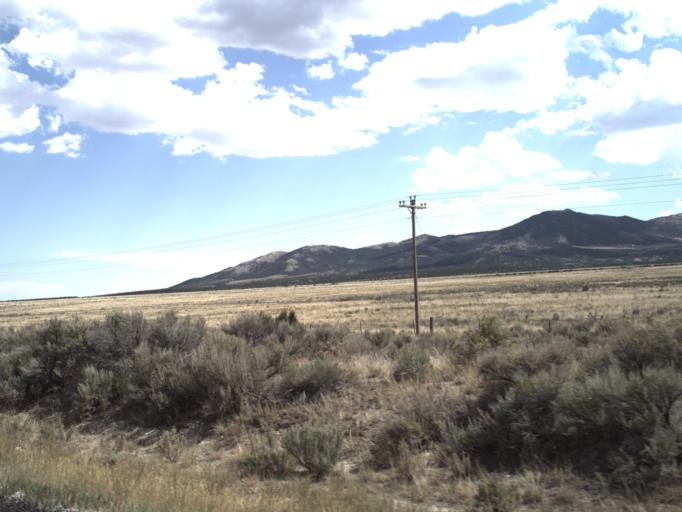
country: US
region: Idaho
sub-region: Minidoka County
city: Rupert
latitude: 41.9930
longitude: -113.1875
